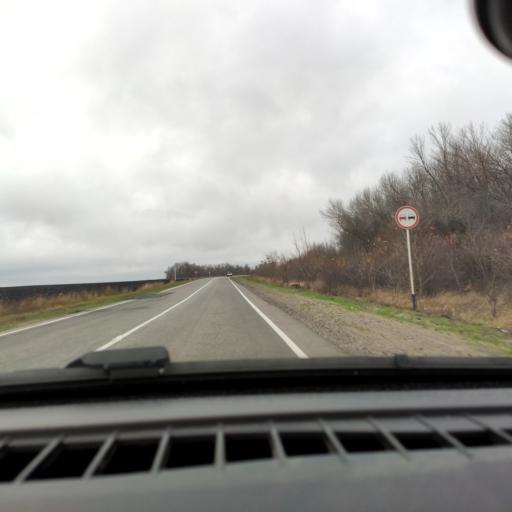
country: RU
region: Voronezj
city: Shilovo
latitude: 51.3873
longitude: 39.0051
